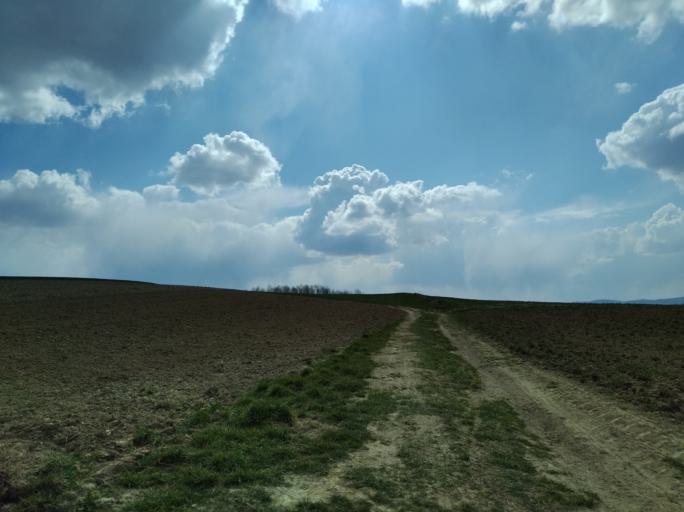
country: PL
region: Subcarpathian Voivodeship
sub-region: Powiat strzyzowski
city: Strzyzow
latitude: 49.9131
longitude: 21.7479
